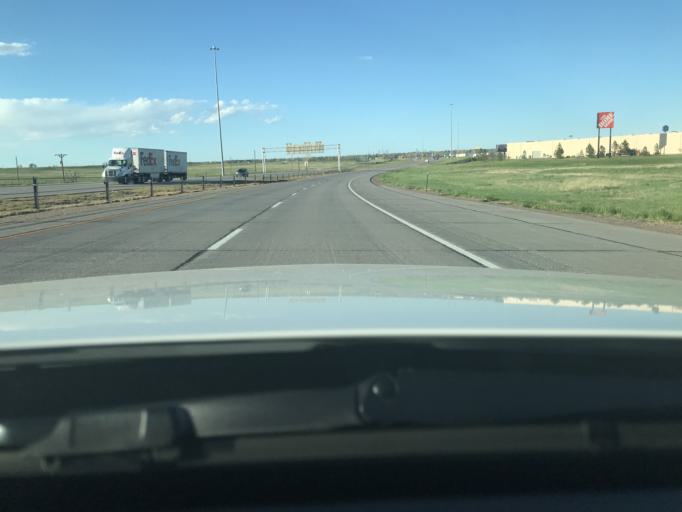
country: US
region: Wyoming
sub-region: Laramie County
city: Cheyenne
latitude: 41.1223
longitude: -104.8501
